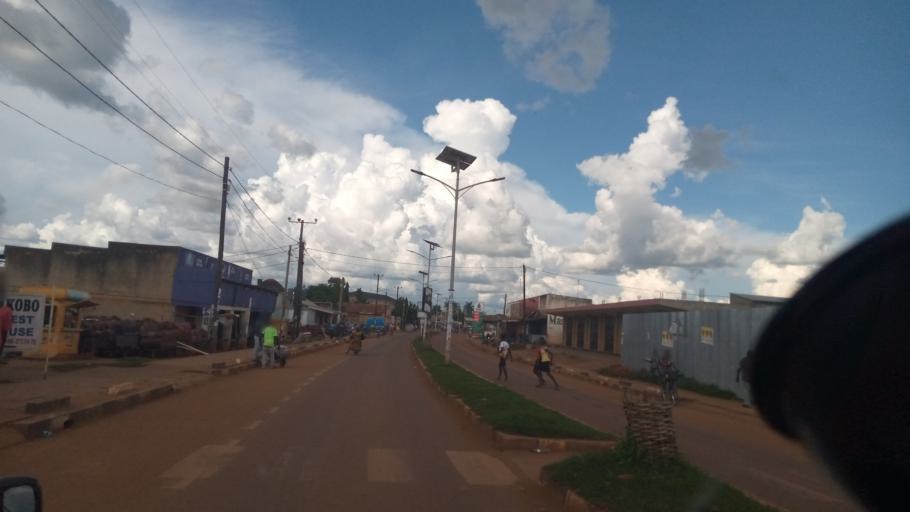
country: UG
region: Northern Region
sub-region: Lira District
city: Lira
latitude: 2.2418
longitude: 32.8905
